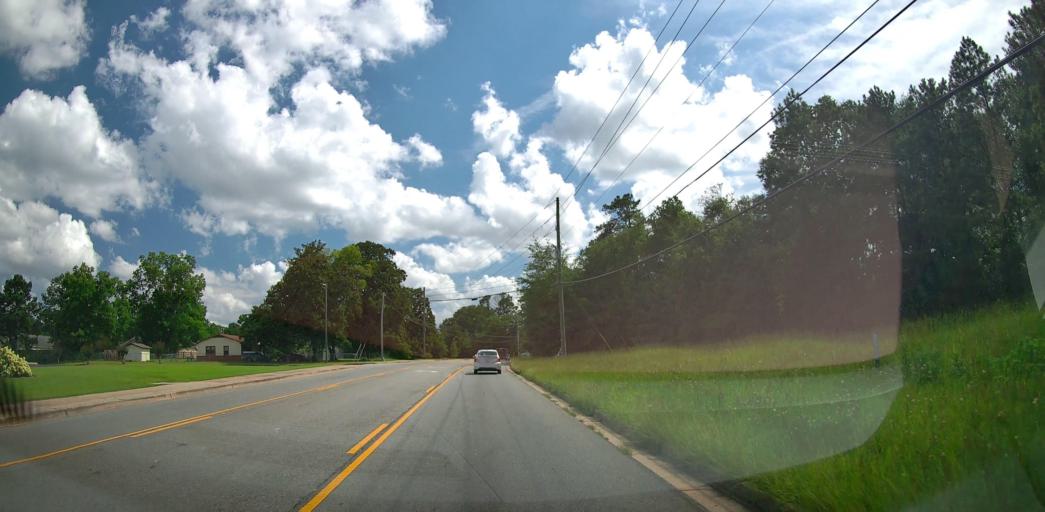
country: US
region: Georgia
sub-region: Houston County
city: Centerville
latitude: 32.6087
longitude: -83.6549
